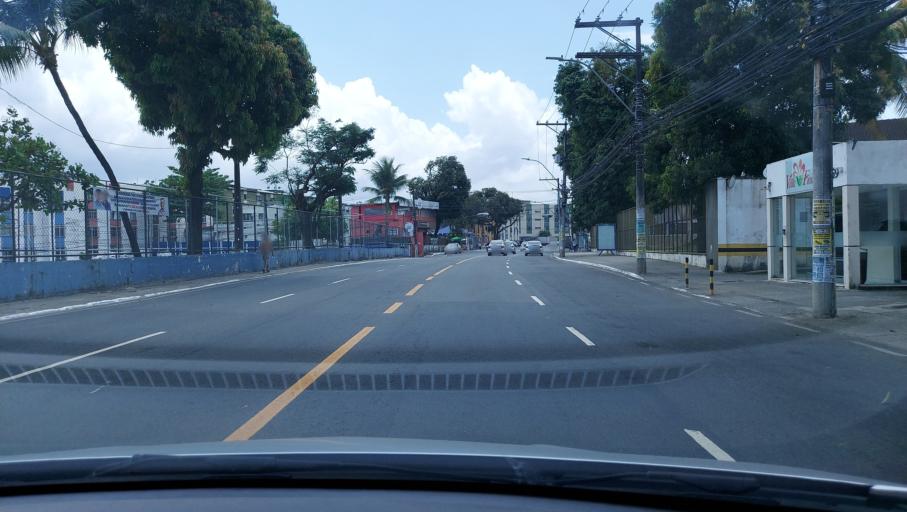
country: BR
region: Bahia
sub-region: Salvador
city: Salvador
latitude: -12.9627
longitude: -38.4717
